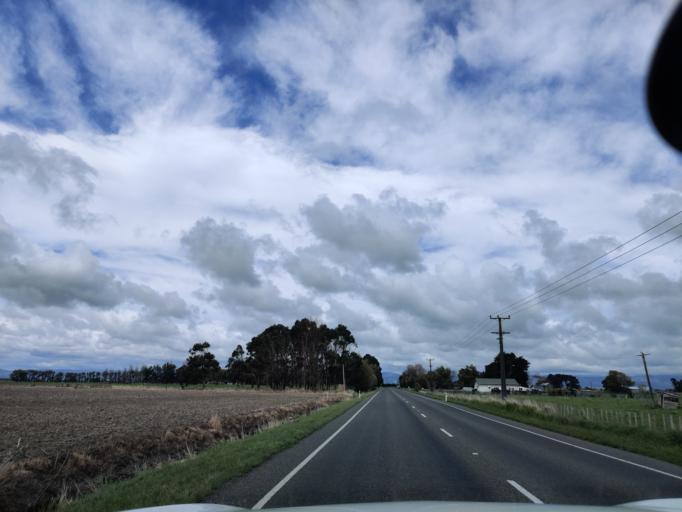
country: NZ
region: Manawatu-Wanganui
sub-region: Palmerston North City
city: Palmerston North
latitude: -40.3243
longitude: 175.5036
